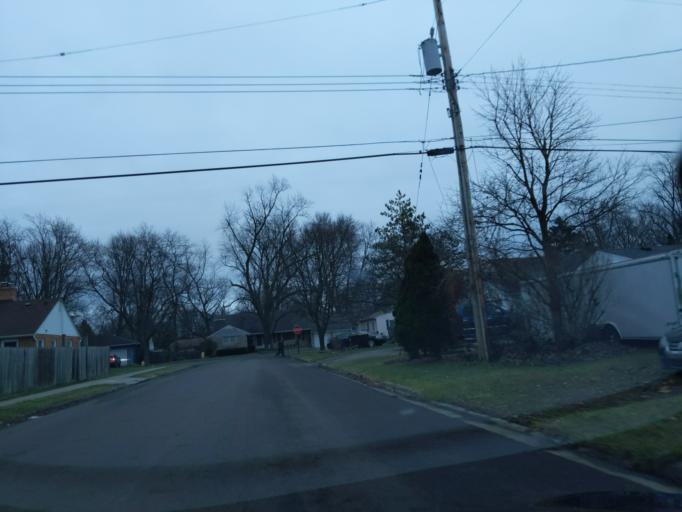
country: US
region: Michigan
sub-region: Eaton County
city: Waverly
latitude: 42.7374
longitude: -84.6180
